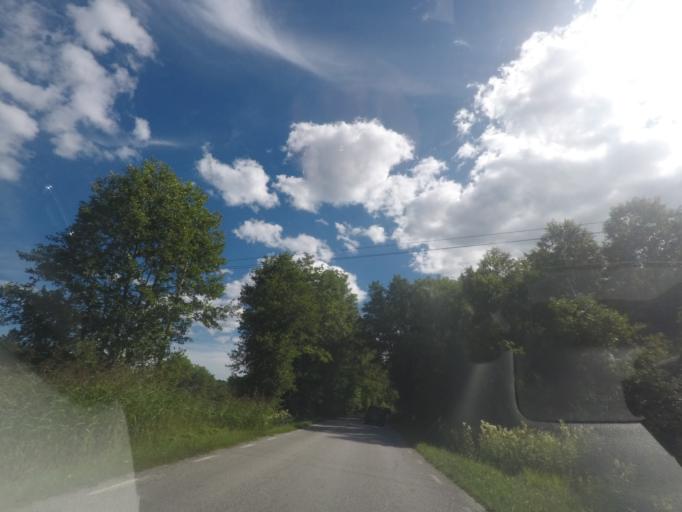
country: SE
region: Stockholm
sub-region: Norrtalje Kommun
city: Arno
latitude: 60.1079
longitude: 18.8076
